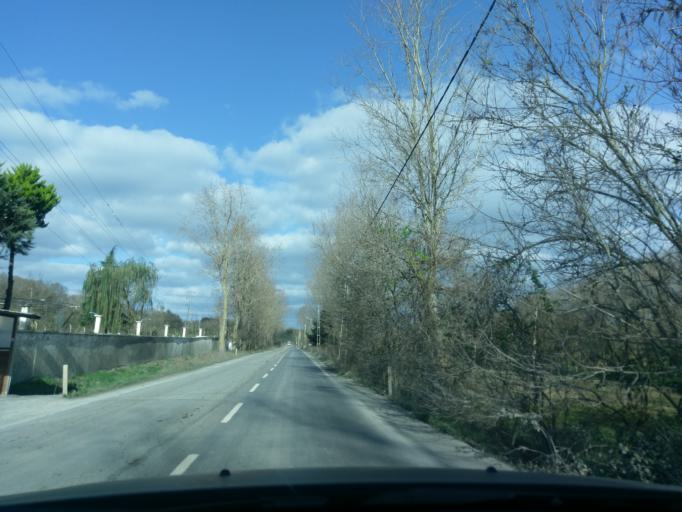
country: TR
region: Istanbul
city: Durusu
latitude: 41.2854
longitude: 28.6640
